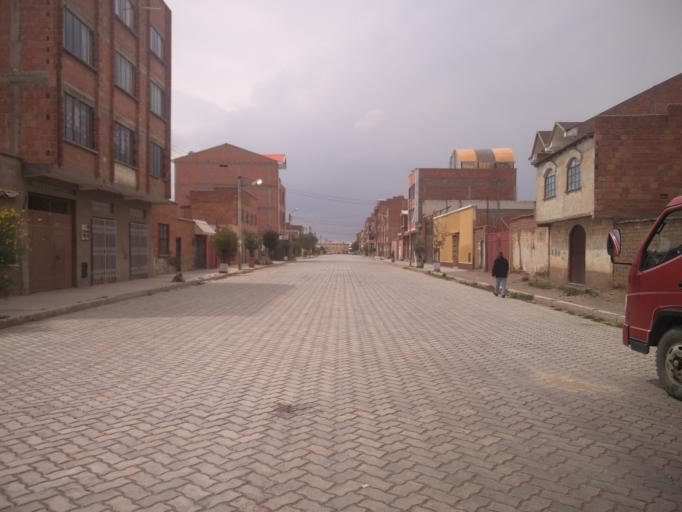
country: BO
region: La Paz
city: La Paz
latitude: -16.5367
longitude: -68.1969
